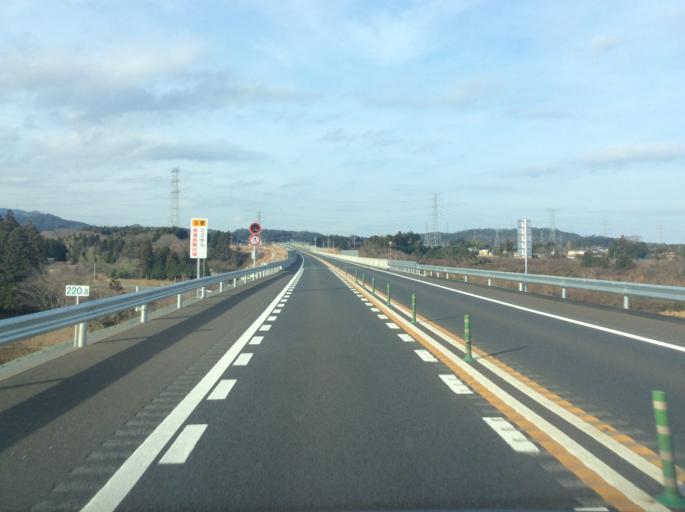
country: JP
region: Fukushima
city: Namie
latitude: 37.3953
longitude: 140.9658
